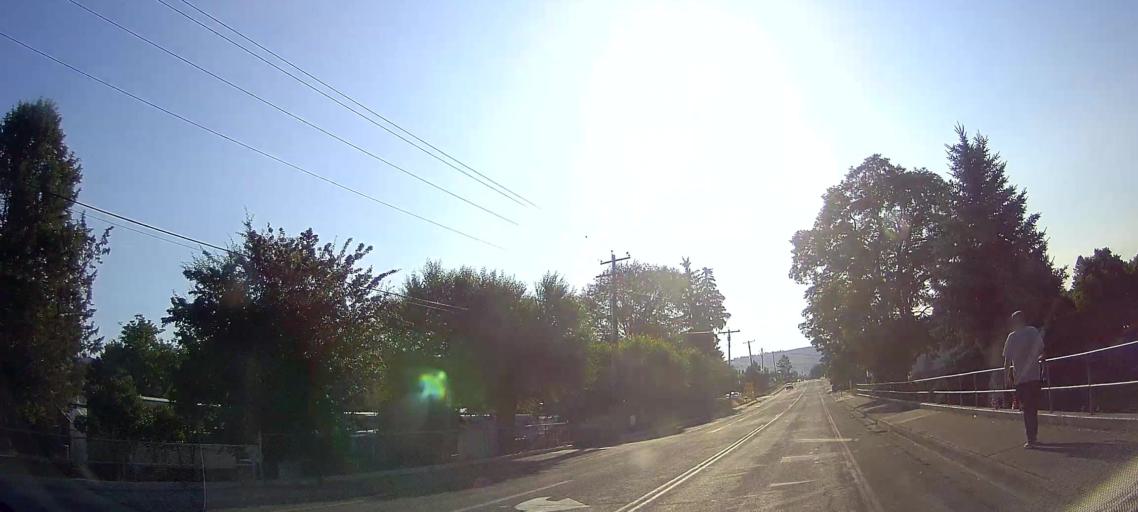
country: US
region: Oregon
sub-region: Klamath County
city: Altamont
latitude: 42.2139
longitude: -121.7486
